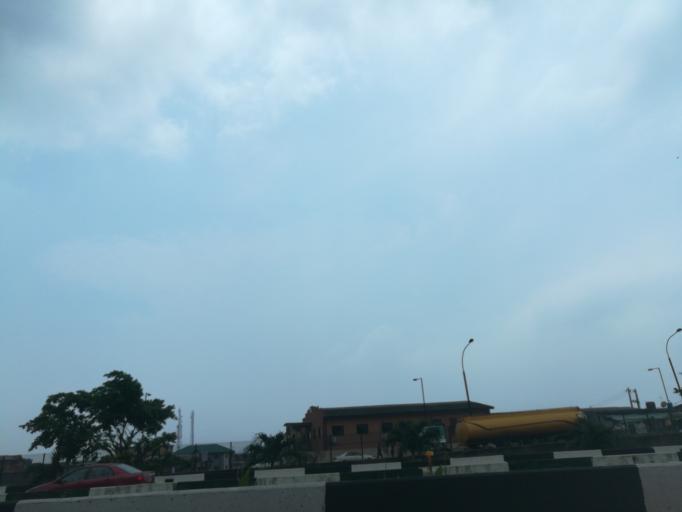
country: NG
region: Lagos
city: Somolu
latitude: 6.5528
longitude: 3.3968
